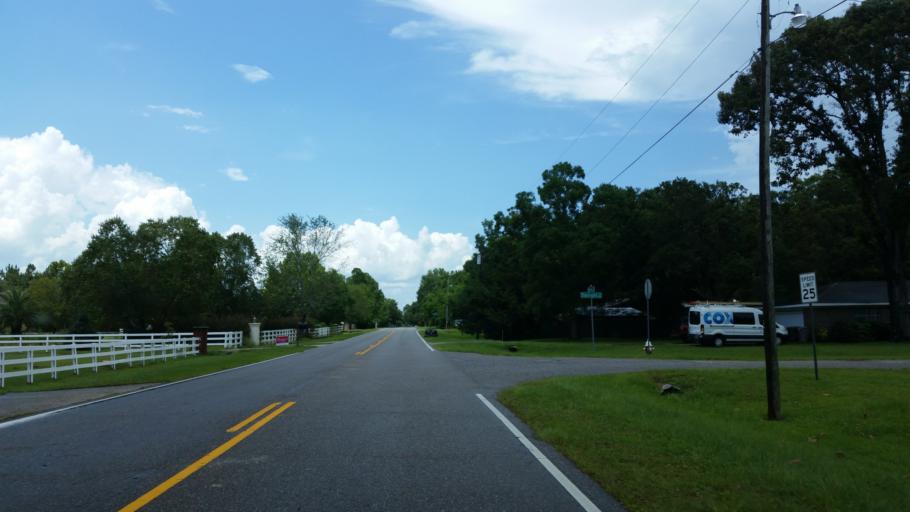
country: US
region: Florida
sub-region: Escambia County
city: Ensley
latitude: 30.5377
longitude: -87.3005
